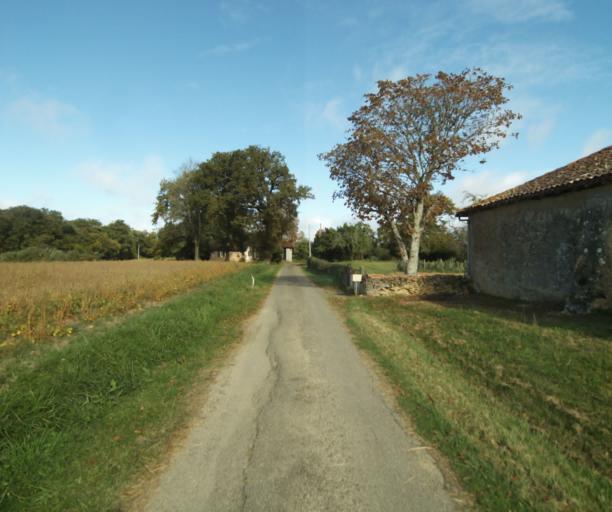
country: FR
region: Midi-Pyrenees
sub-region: Departement du Gers
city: Nogaro
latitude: 43.8470
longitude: -0.0454
